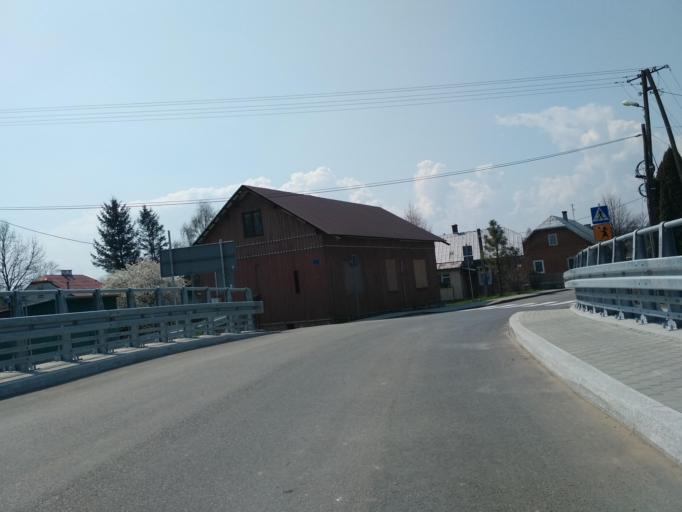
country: PL
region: Subcarpathian Voivodeship
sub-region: Powiat sanocki
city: Zarszyn
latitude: 49.5808
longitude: 22.0142
